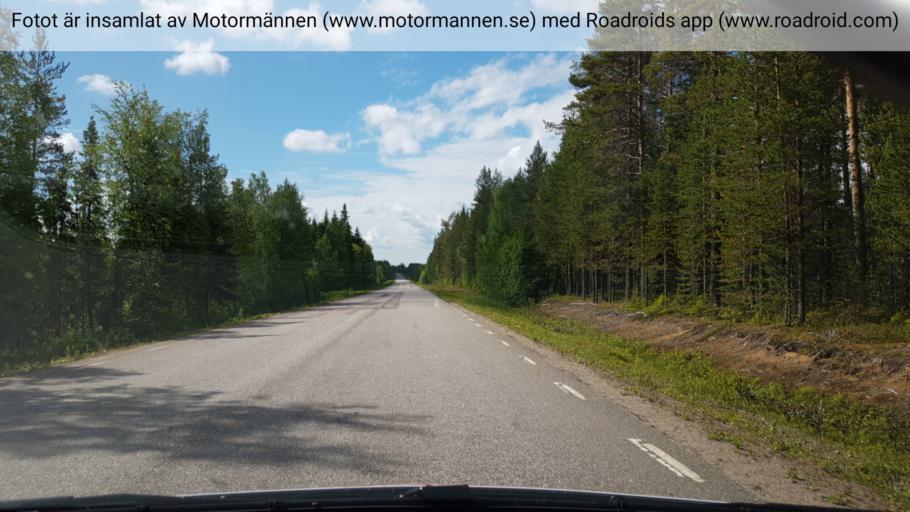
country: FI
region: Lapland
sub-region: Torniolaakso
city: Pello
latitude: 66.7784
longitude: 23.8869
